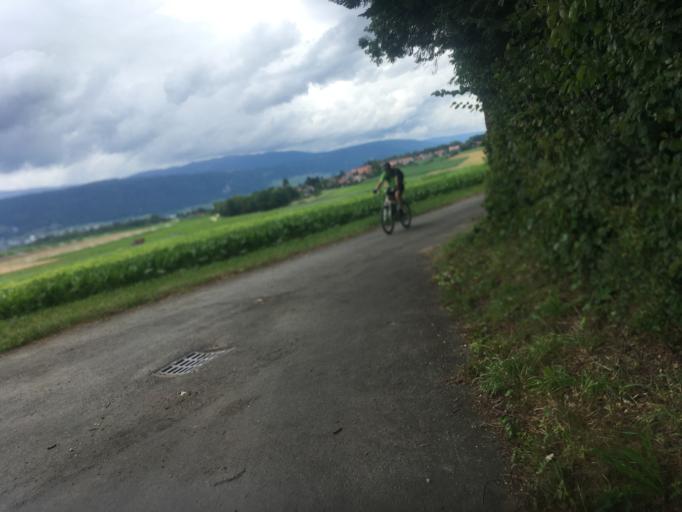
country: CH
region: Bern
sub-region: Seeland District
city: Ins
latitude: 47.0219
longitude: 7.1024
